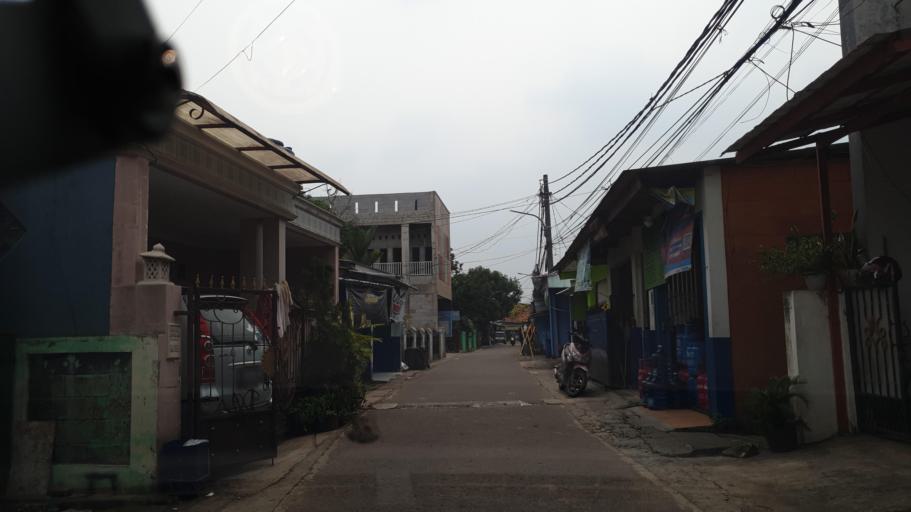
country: ID
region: West Java
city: Pamulang
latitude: -6.3306
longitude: 106.7709
